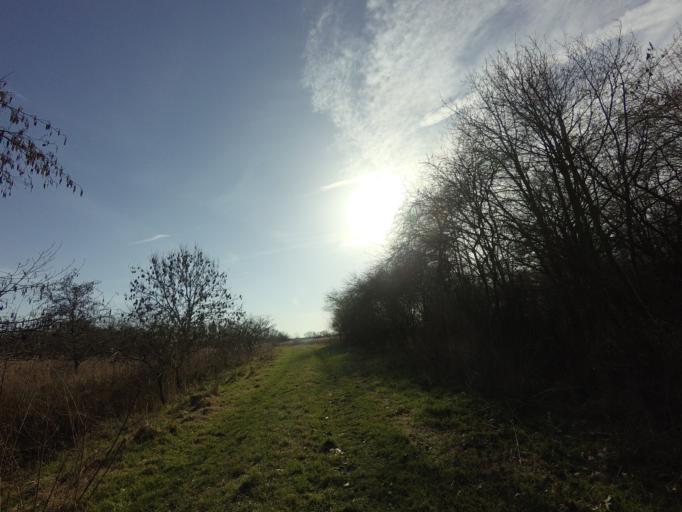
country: NL
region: North Holland
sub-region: Gemeente Naarden
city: Naarden
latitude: 52.3361
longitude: 5.1708
